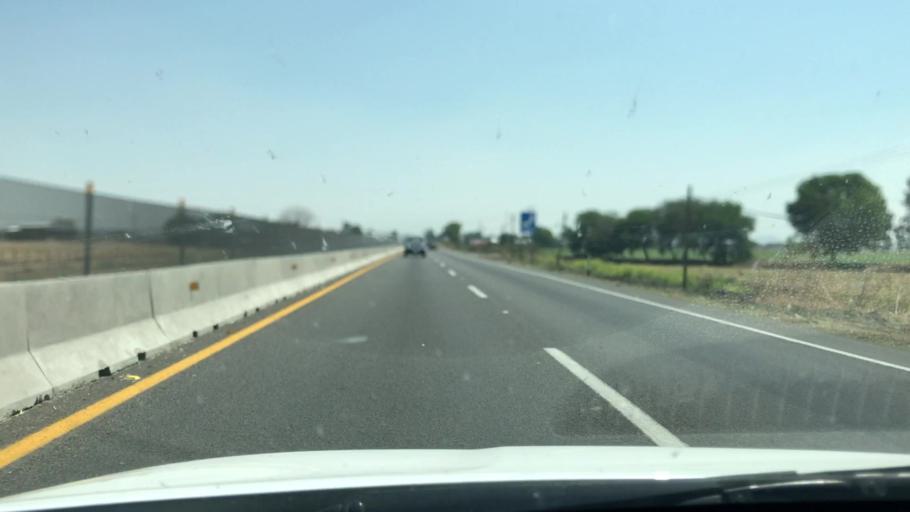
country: MX
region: Guanajuato
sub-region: Abasolo
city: San Bernardo Pena Blanca
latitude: 20.4842
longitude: -101.4929
